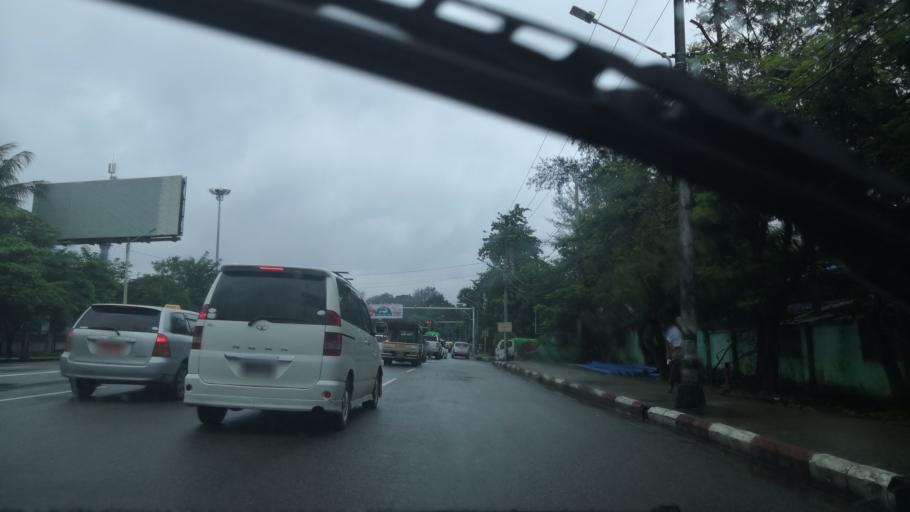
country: MM
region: Yangon
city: Yangon
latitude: 16.8891
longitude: 96.1224
